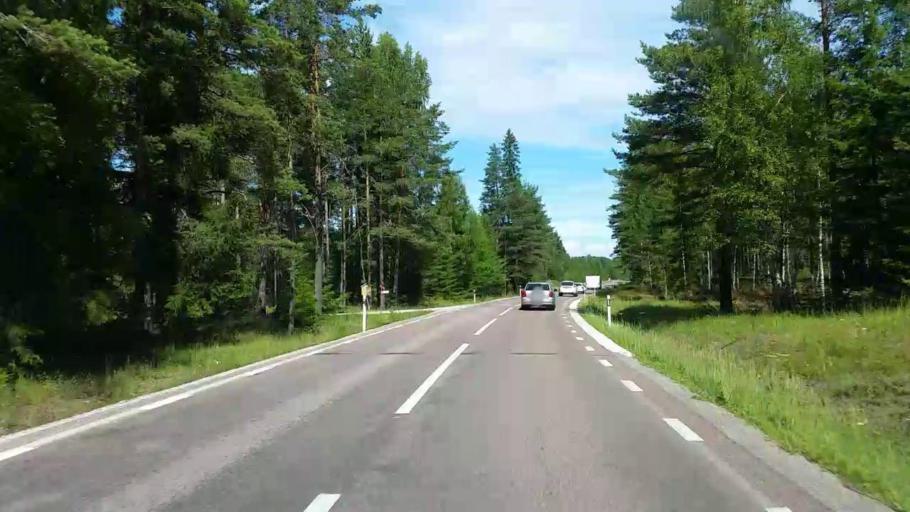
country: SE
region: Dalarna
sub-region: Rattviks Kommun
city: Raettvik
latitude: 60.9160
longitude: 15.2034
